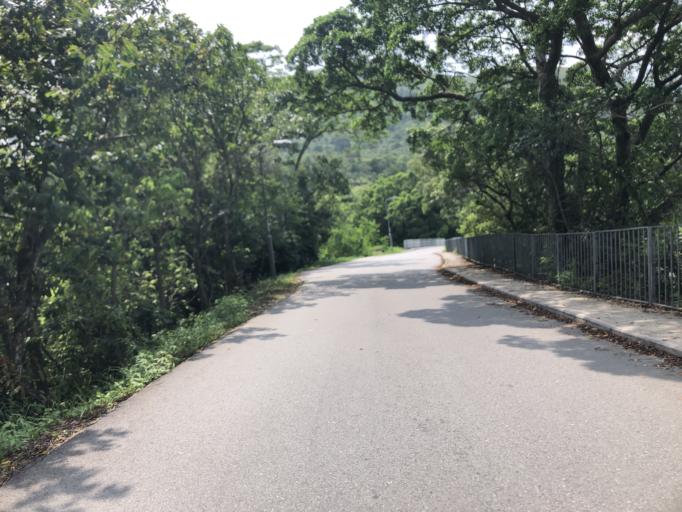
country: CN
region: Guangdong
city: Haishan
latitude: 22.5241
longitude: 114.2098
